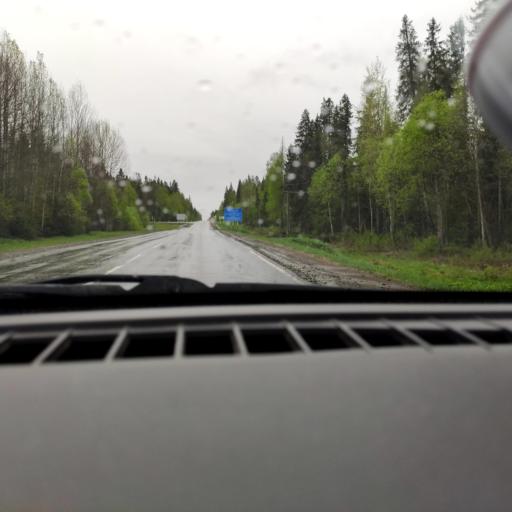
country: RU
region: Perm
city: Perm
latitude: 58.1994
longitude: 56.2068
